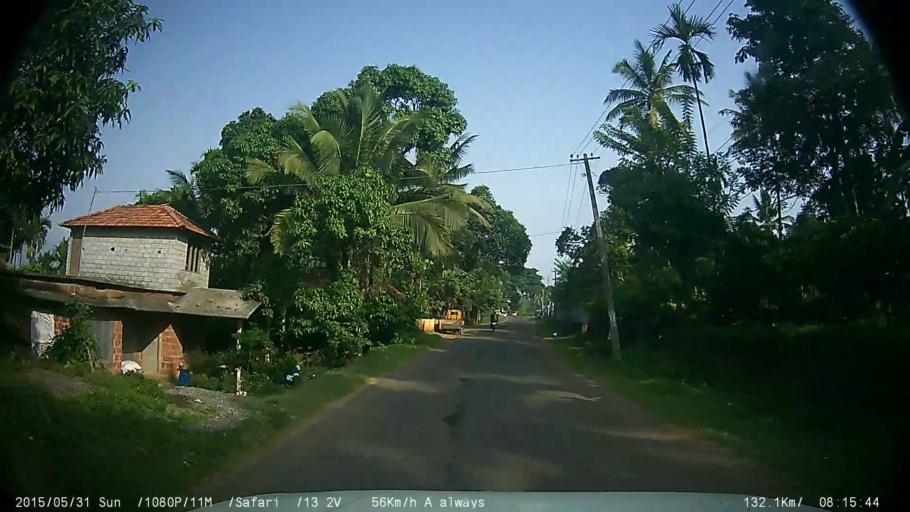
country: IN
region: Kerala
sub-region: Wayanad
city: Kalpetta
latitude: 11.6517
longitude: 76.0012
